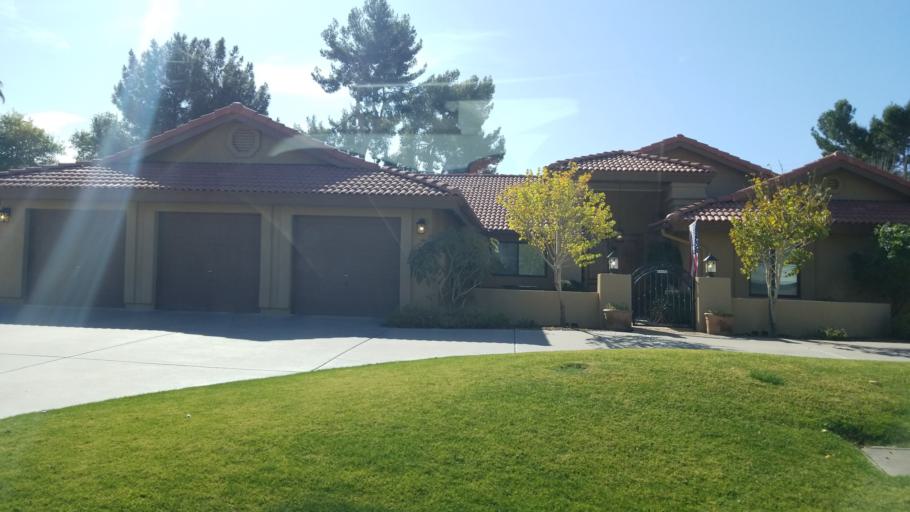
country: US
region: Arizona
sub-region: Maricopa County
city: Paradise Valley
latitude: 33.5862
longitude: -111.9830
